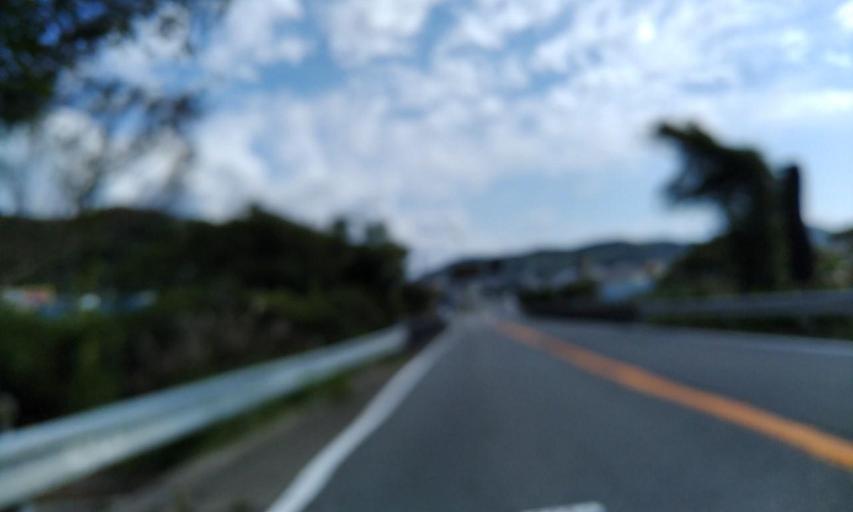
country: JP
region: Wakayama
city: Gobo
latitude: 33.9331
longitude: 135.1402
